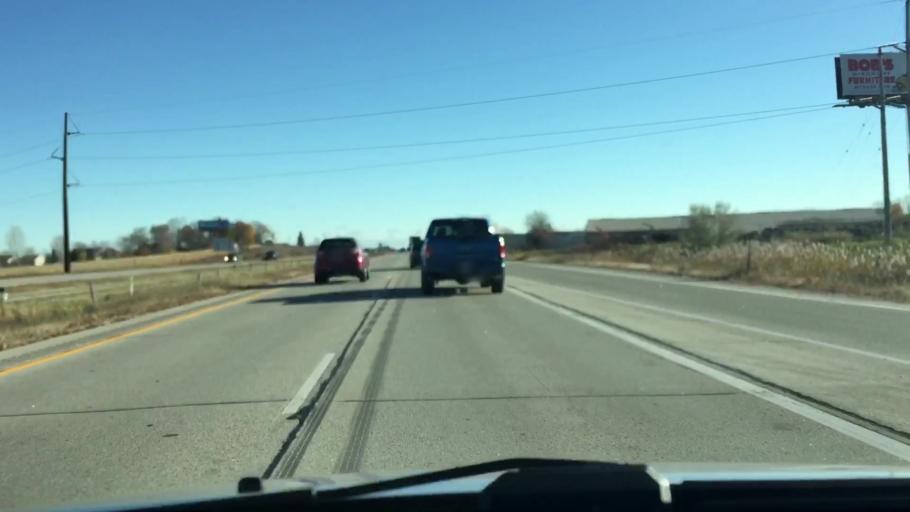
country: US
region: Wisconsin
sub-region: Outagamie County
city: Kaukauna
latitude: 44.3062
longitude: -88.2467
